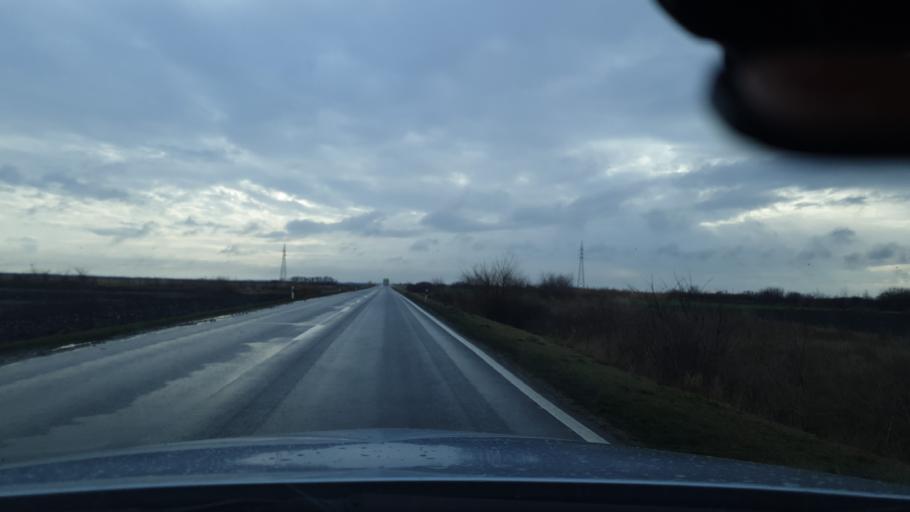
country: RS
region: Autonomna Pokrajina Vojvodina
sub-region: Juznobanatski Okrug
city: Kovin
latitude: 44.7986
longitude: 20.9058
